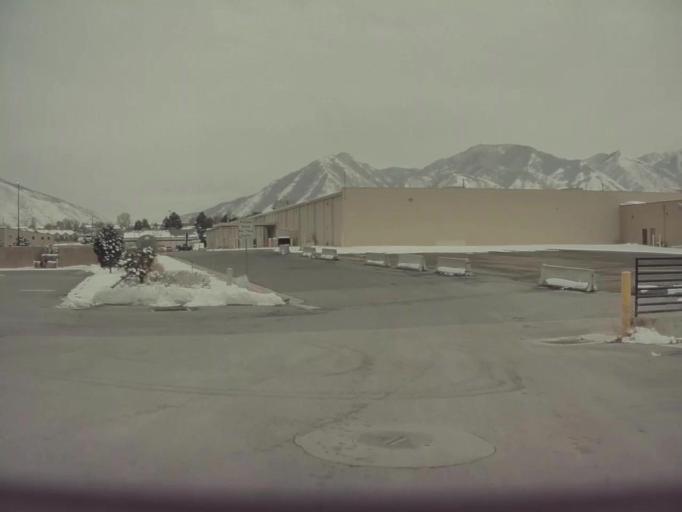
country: US
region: Utah
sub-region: Utah County
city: Spanish Fork
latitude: 40.1234
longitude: -111.6401
